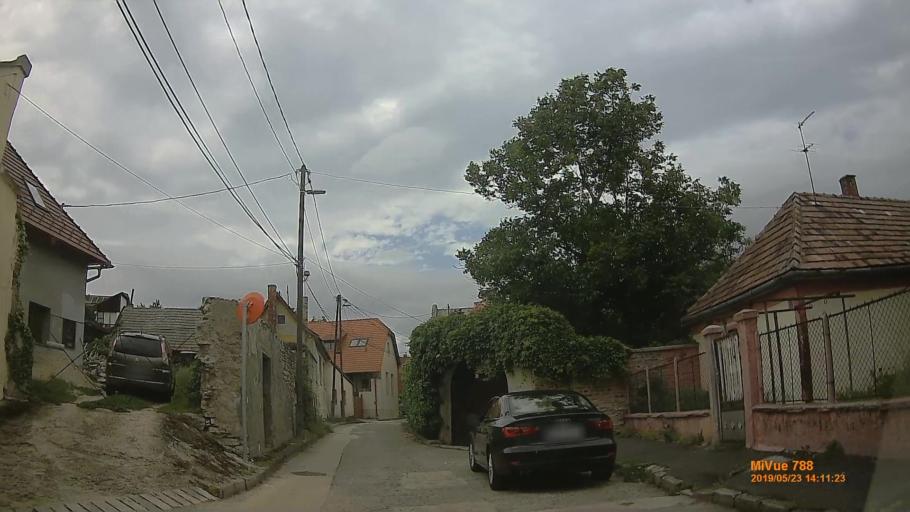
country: HU
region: Veszprem
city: Veszprem
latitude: 47.0986
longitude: 17.9004
